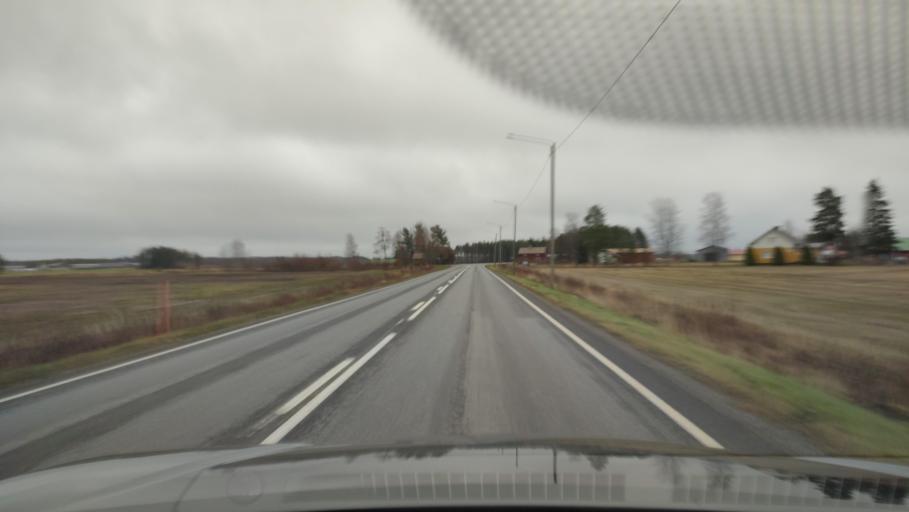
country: FI
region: Southern Ostrobothnia
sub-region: Suupohja
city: Isojoki
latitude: 62.1809
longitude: 21.8269
